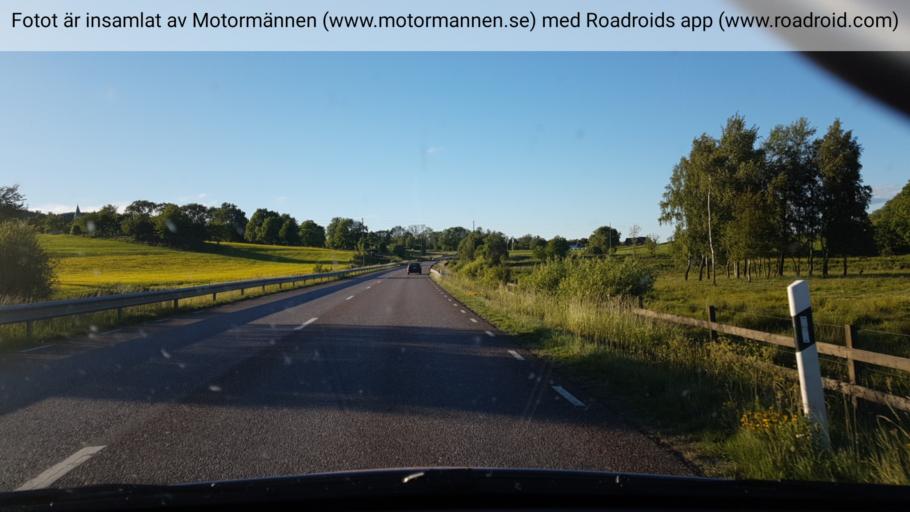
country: SE
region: Vaestra Goetaland
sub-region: Skovde Kommun
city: Skultorp
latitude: 58.2876
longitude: 13.8051
